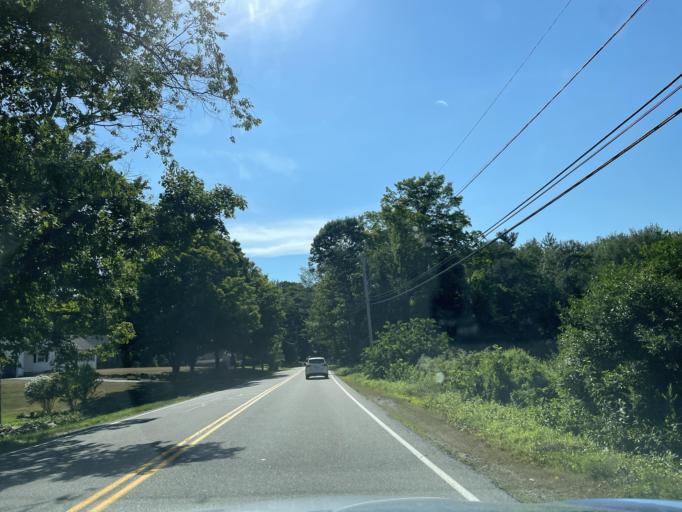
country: US
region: Massachusetts
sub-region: Worcester County
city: Sutton
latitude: 42.1513
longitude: -71.7106
